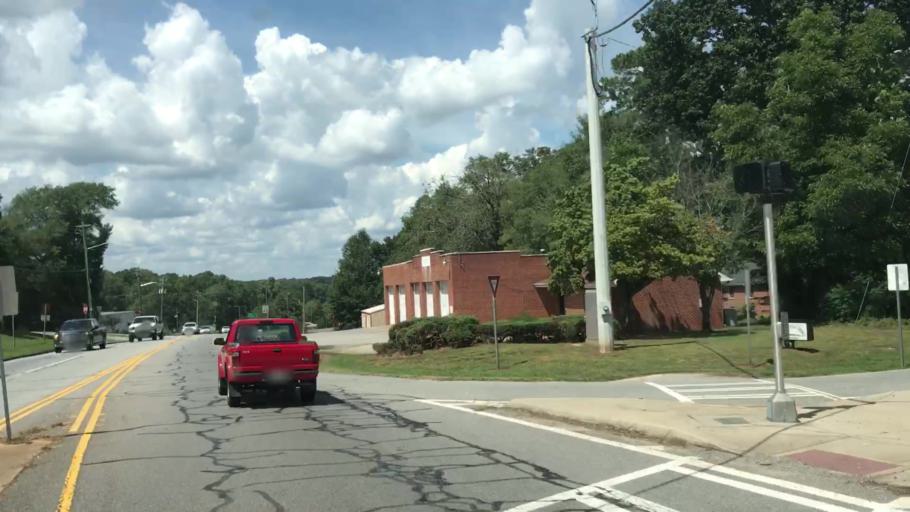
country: US
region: Georgia
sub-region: Oconee County
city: Watkinsville
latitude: 33.8654
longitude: -83.4109
